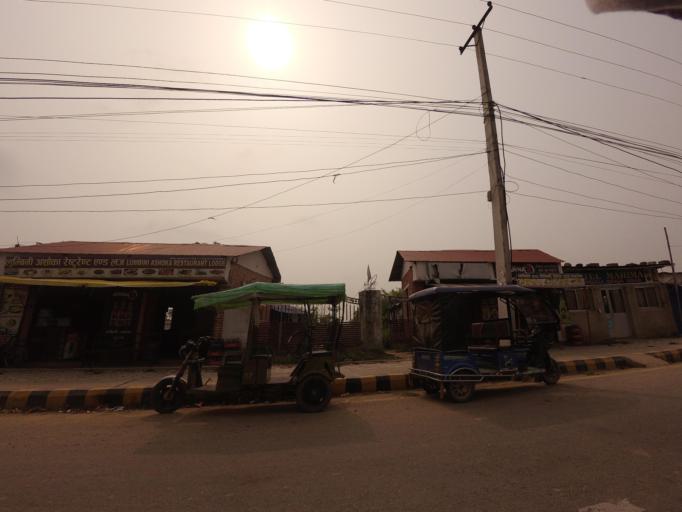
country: IN
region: Uttar Pradesh
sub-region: Maharajganj
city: Nautanwa
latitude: 27.4743
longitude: 83.2840
